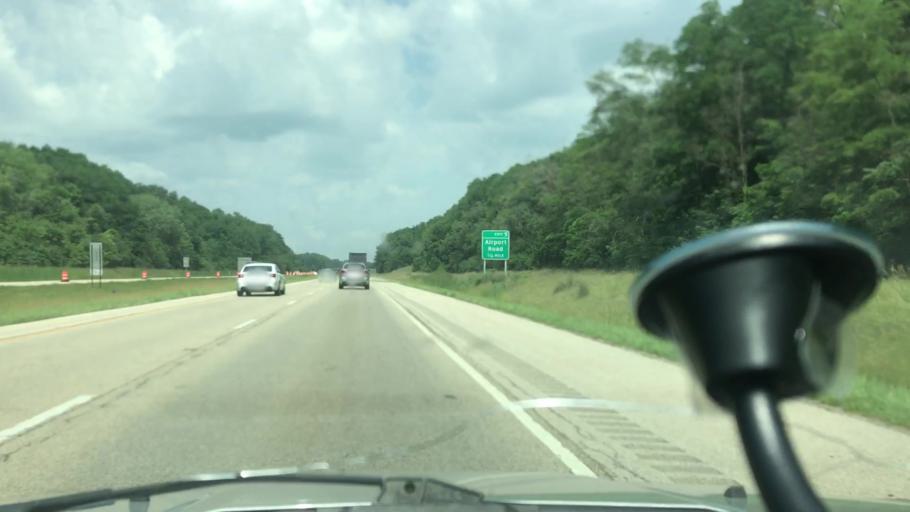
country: US
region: Illinois
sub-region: Peoria County
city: Bartonville
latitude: 40.6657
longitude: -89.6569
